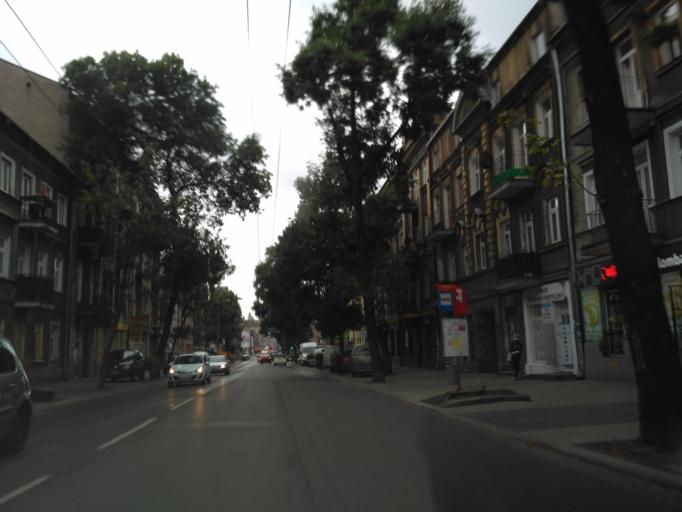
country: PL
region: Lublin Voivodeship
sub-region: Powiat lubelski
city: Lublin
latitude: 51.2548
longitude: 22.5699
